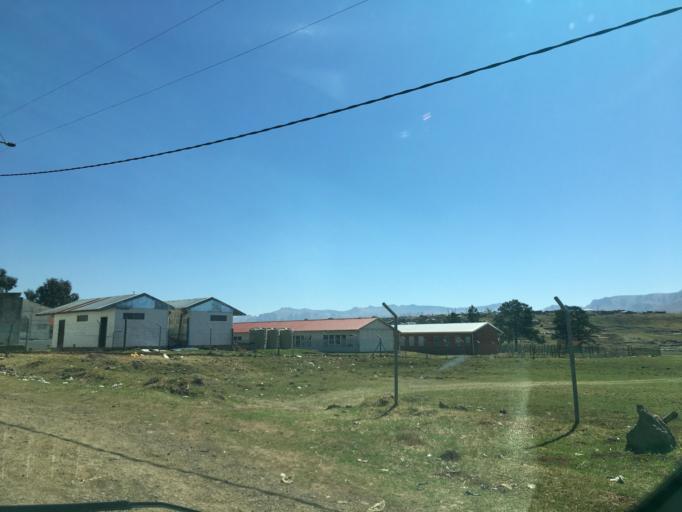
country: ZA
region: Eastern Cape
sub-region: Chris Hani District Municipality
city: Elliot
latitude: -31.3297
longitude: 27.8272
